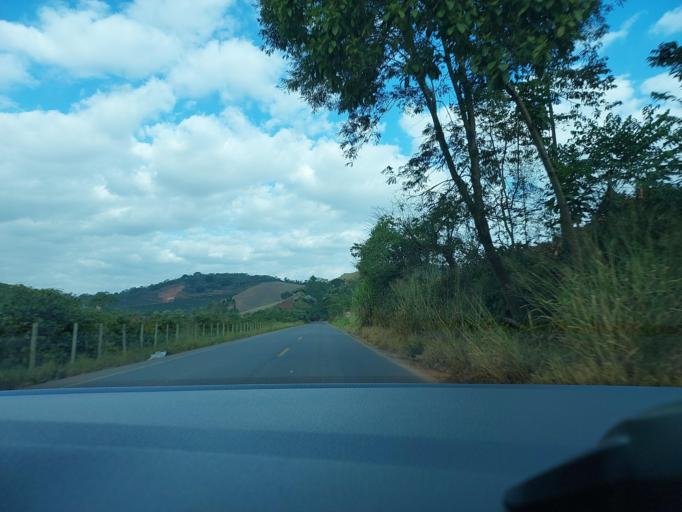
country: BR
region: Minas Gerais
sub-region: Vicosa
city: Vicosa
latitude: -20.8395
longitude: -42.6889
